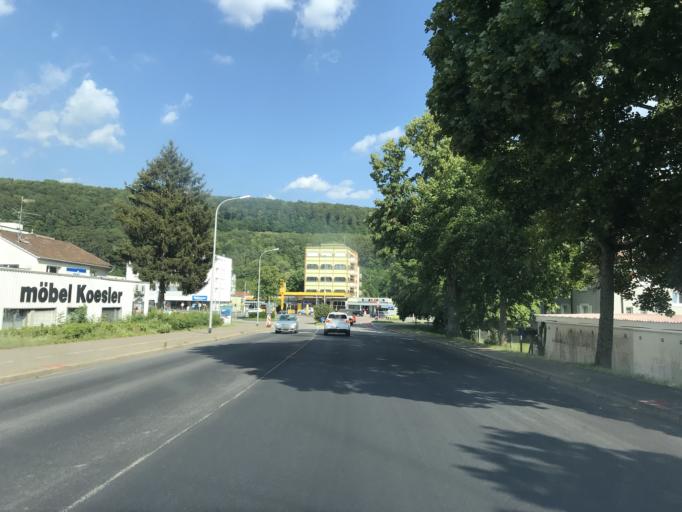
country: DE
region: Baden-Wuerttemberg
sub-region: Freiburg Region
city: Loerrach
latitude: 47.6232
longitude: 7.6738
